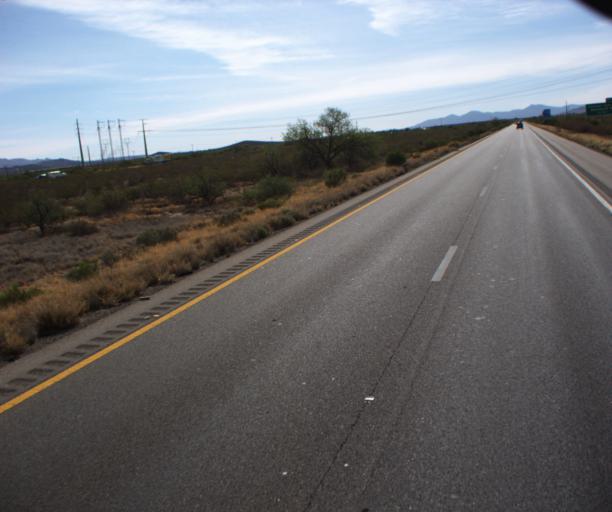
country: US
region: Arizona
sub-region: Pima County
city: Vail
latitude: 32.0346
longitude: -110.7320
